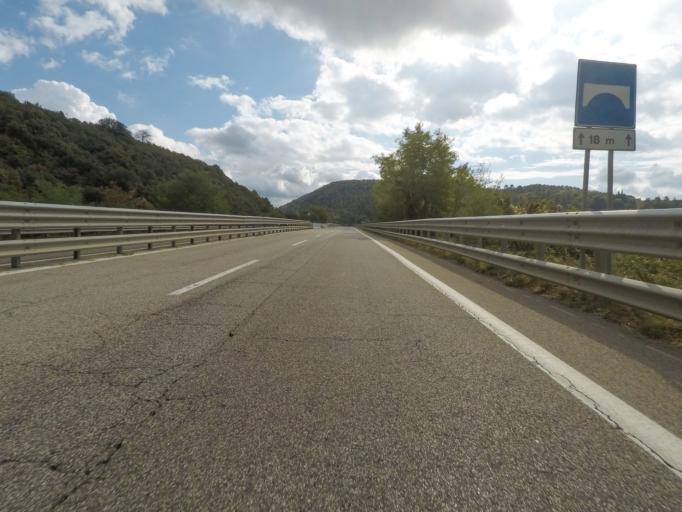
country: IT
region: Tuscany
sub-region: Provincia di Siena
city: Rapolano Terme
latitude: 43.2928
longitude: 11.6089
